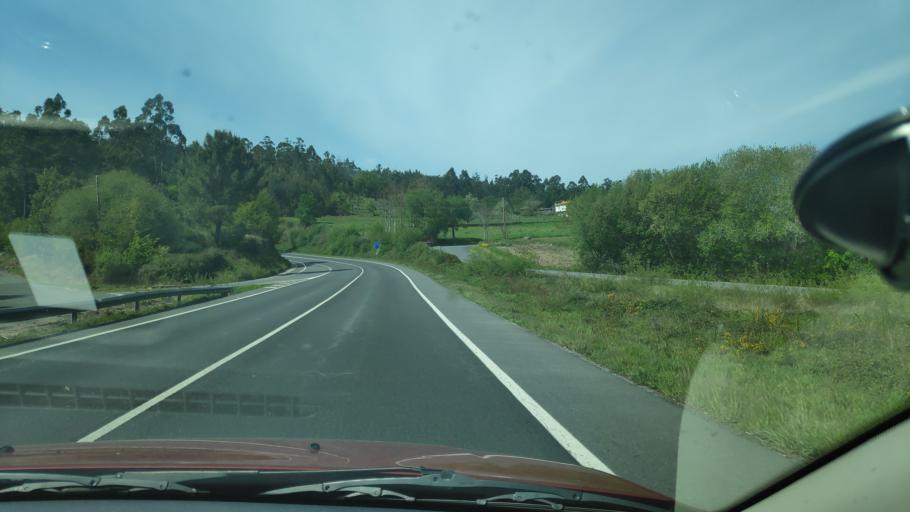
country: ES
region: Galicia
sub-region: Provincia da Coruna
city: Ames
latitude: 42.8781
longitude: -8.6627
